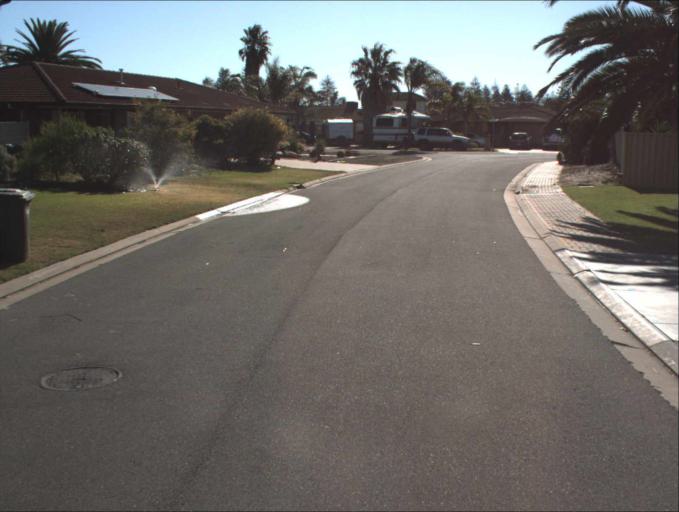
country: AU
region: South Australia
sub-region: Port Adelaide Enfield
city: Birkenhead
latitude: -34.7836
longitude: 138.4943
